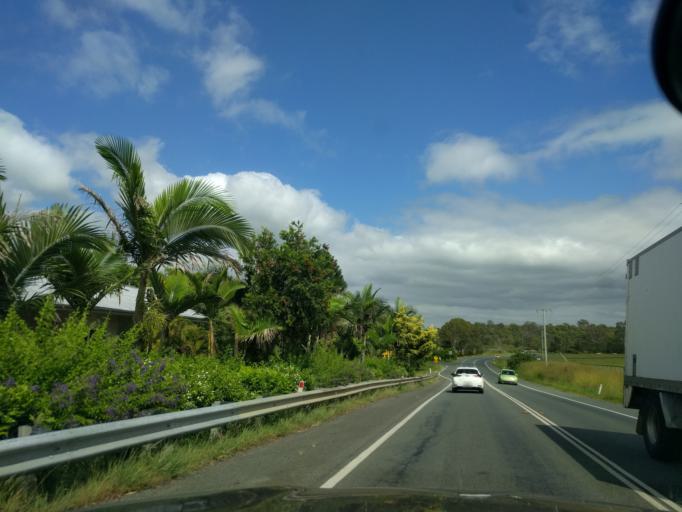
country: AU
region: Queensland
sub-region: Logan
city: Cedar Vale
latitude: -27.9078
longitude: 152.9788
